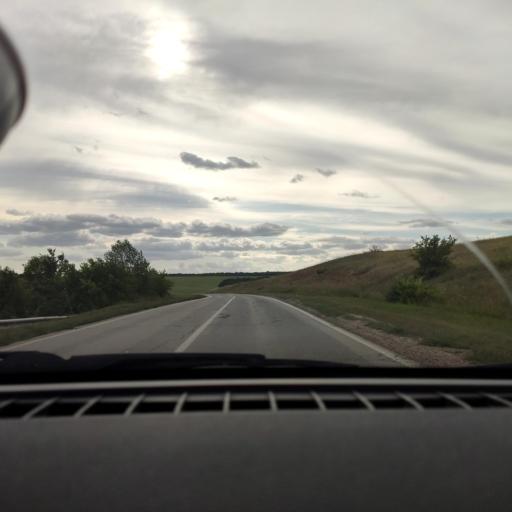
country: RU
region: Samara
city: Krasnyy Yar
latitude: 53.4378
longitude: 50.5802
